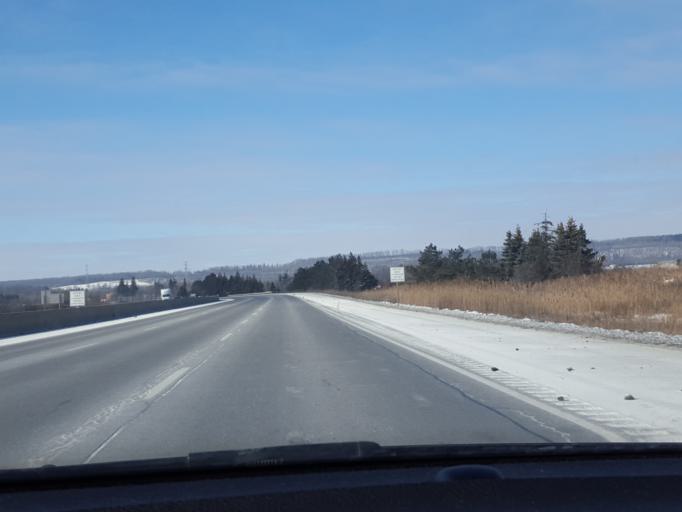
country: CA
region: Ontario
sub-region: Halton
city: Milton
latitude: 43.5248
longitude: -79.9252
